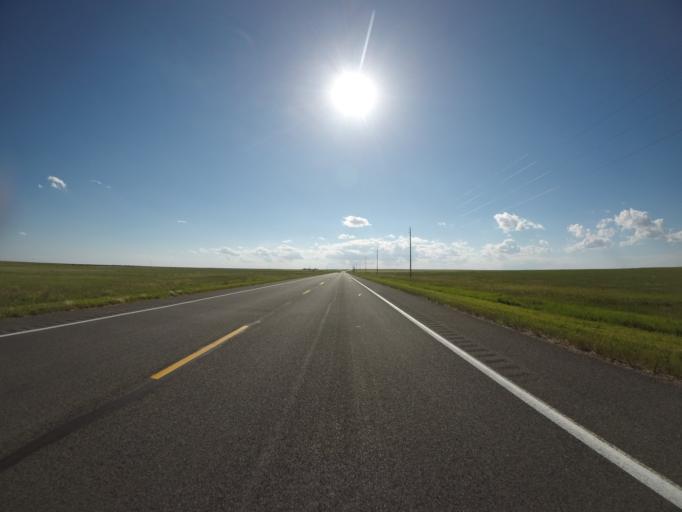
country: US
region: Colorado
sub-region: Morgan County
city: Brush
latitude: 40.6097
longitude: -103.6897
